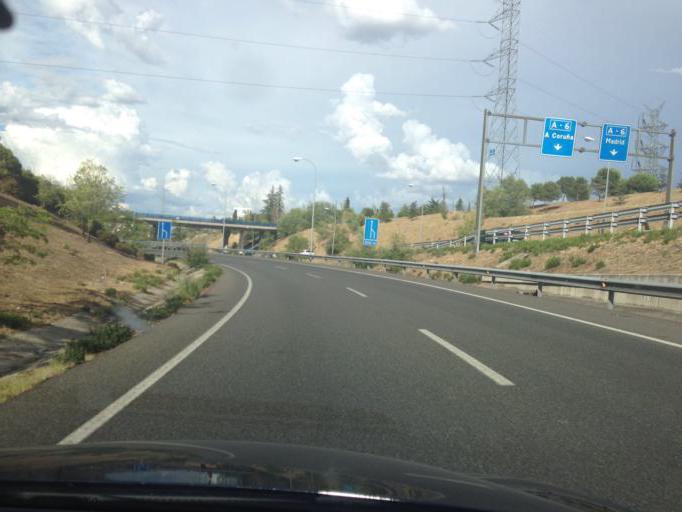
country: ES
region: Madrid
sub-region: Provincia de Madrid
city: Pozuelo de Alarcon
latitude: 40.4626
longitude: -3.7981
